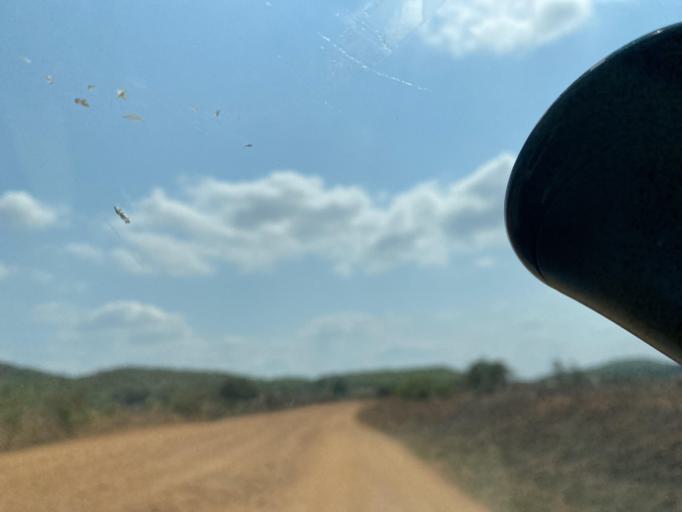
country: ZM
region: Lusaka
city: Chongwe
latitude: -15.6027
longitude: 28.7487
